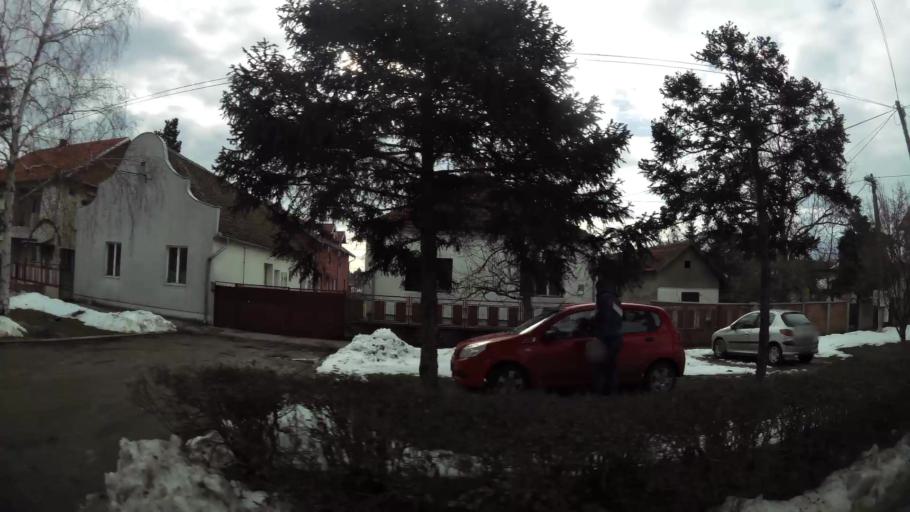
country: RS
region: Central Serbia
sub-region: Belgrade
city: Surcin
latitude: 44.7960
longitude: 20.2819
